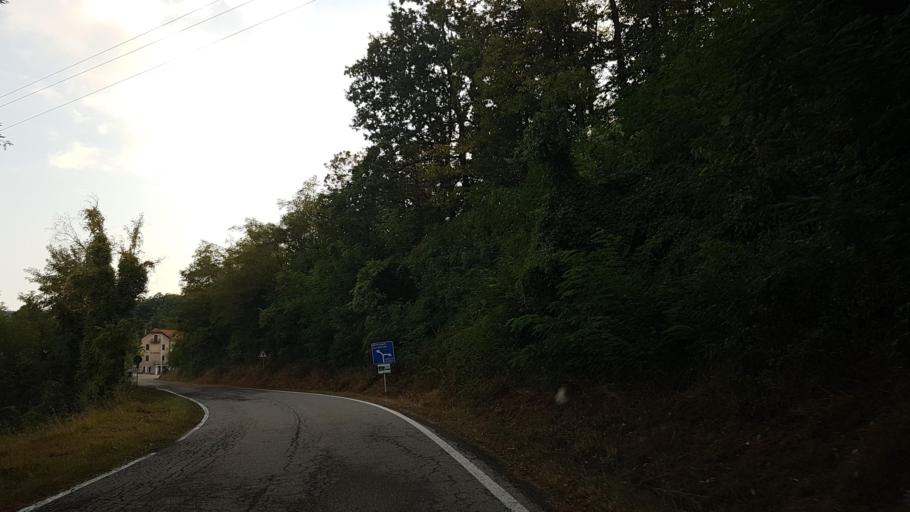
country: IT
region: Emilia-Romagna
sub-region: Provincia di Parma
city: Tornolo
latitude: 44.4401
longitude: 9.6354
